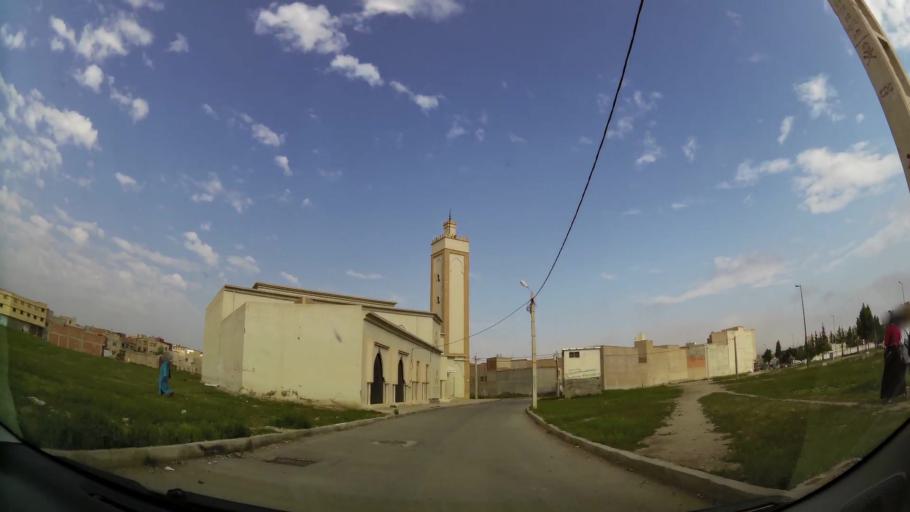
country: MA
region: Oriental
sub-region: Oujda-Angad
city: Oujda
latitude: 34.6922
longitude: -1.9000
